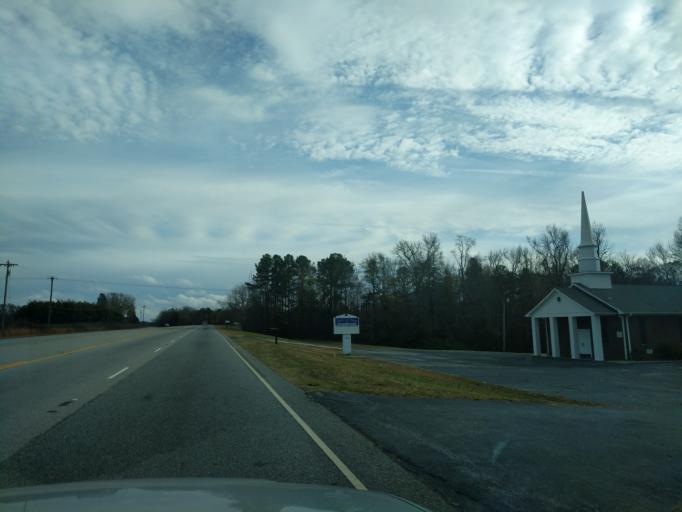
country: US
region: South Carolina
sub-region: Anderson County
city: Honea Path
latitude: 34.5634
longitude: -82.3282
